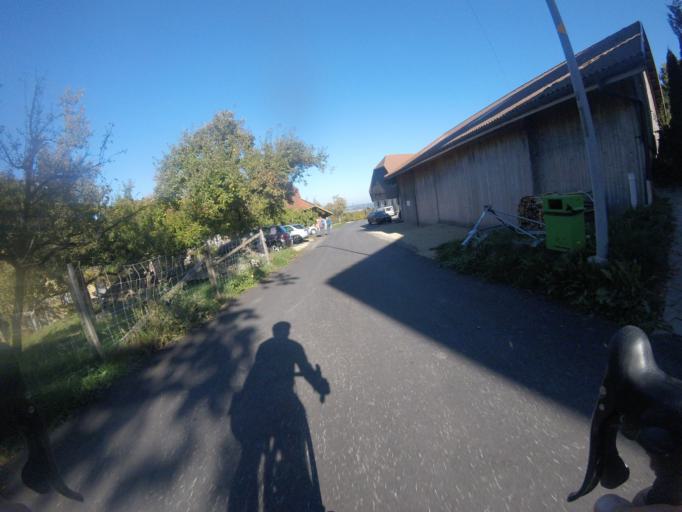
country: CH
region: Bern
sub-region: Seeland District
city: Seedorf
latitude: 47.0328
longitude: 7.3443
